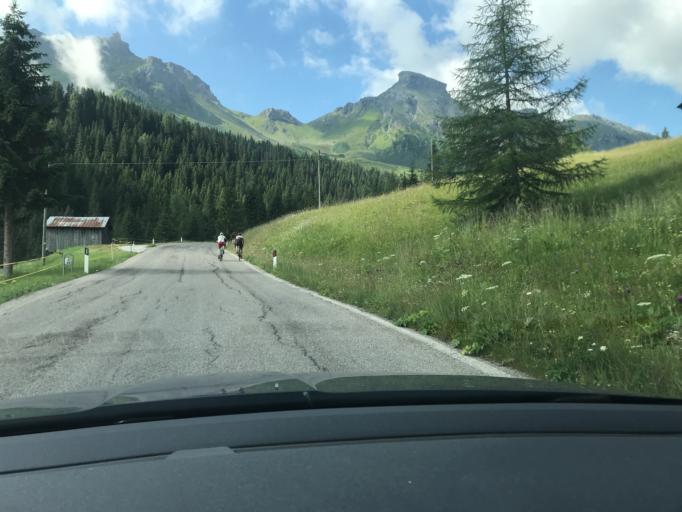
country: IT
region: Trentino-Alto Adige
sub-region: Bolzano
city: Corvara in Badia
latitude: 46.4929
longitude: 11.8553
